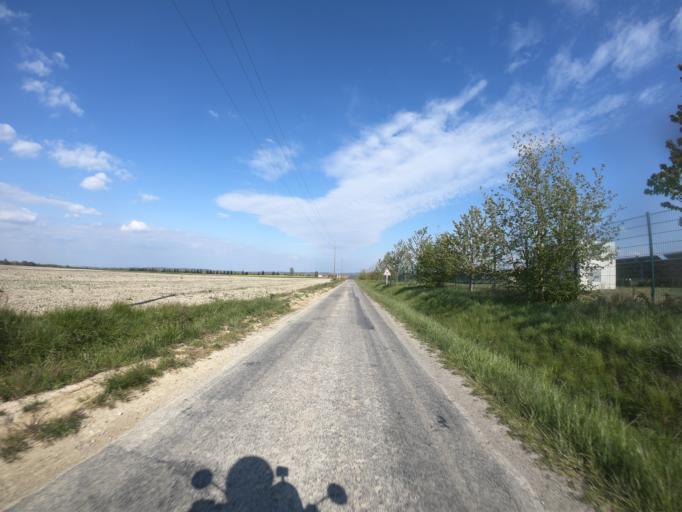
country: FR
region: Midi-Pyrenees
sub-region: Departement de l'Ariege
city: La Tour-du-Crieu
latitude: 43.1078
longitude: 1.6971
